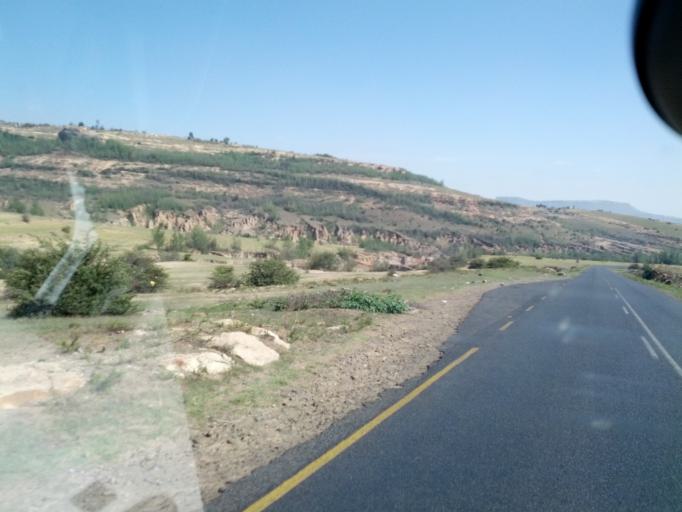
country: LS
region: Berea
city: Teyateyaneng
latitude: -29.1427
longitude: 27.7042
